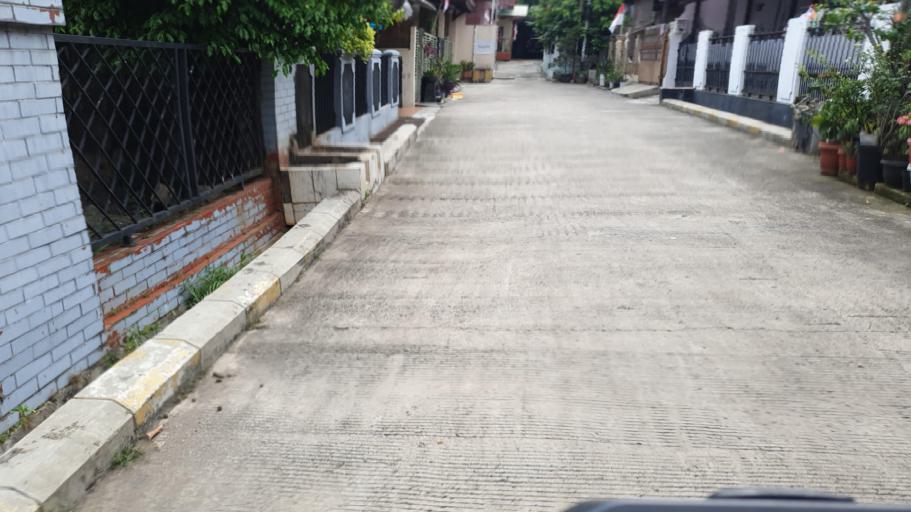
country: ID
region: West Java
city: Depok
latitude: -6.3704
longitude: 106.8525
